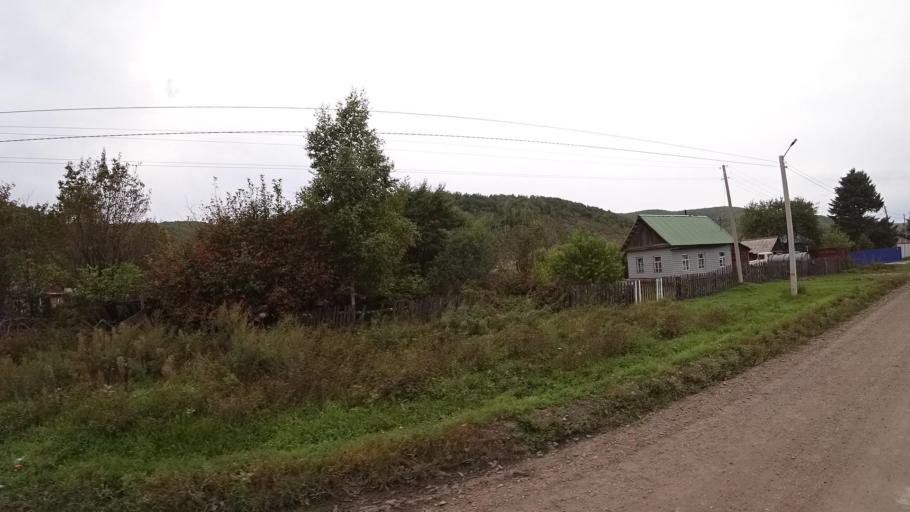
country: RU
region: Jewish Autonomous Oblast
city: Khingansk
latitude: 49.0259
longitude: 131.0479
